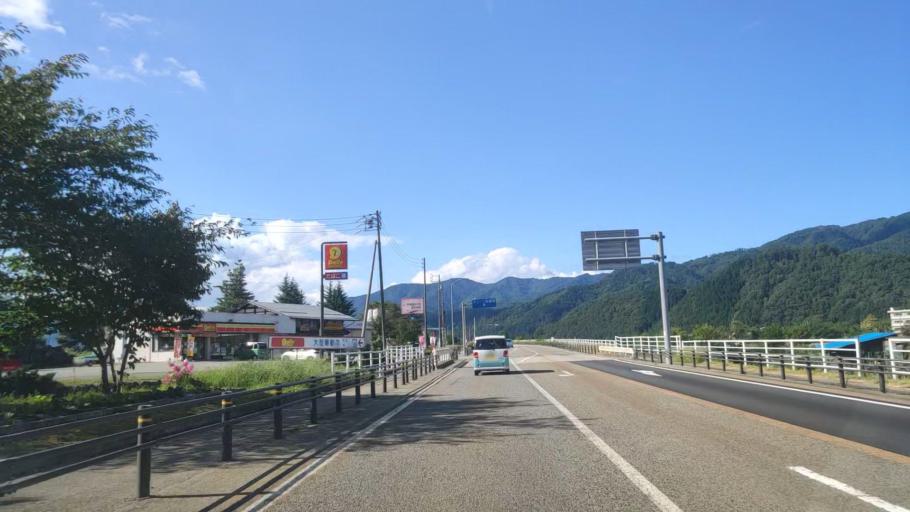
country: JP
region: Gifu
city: Takayama
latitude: 36.2405
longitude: 137.1737
